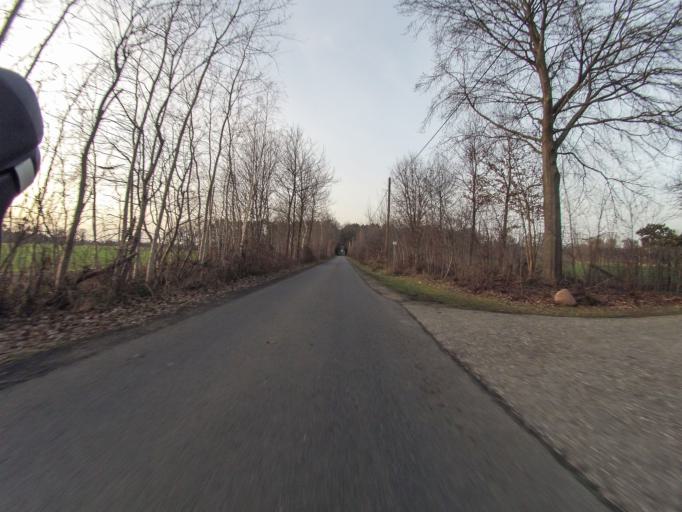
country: DE
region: North Rhine-Westphalia
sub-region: Regierungsbezirk Munster
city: Steinfurt
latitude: 52.1737
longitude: 7.3340
